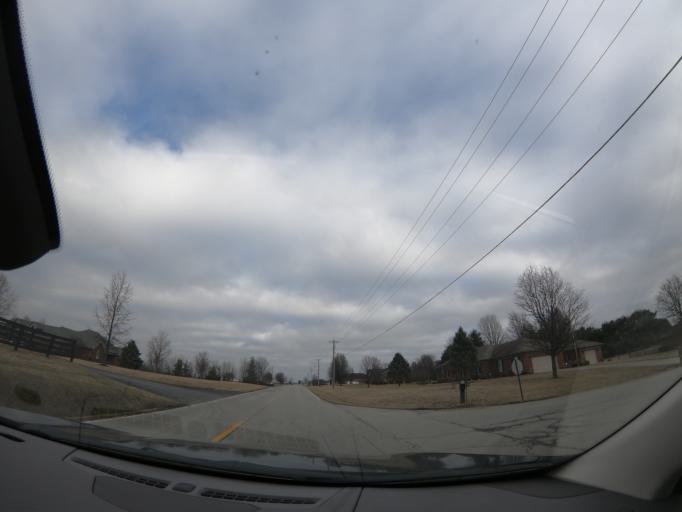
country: US
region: Kentucky
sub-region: Nelson County
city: Bardstown
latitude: 37.8360
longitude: -85.3927
